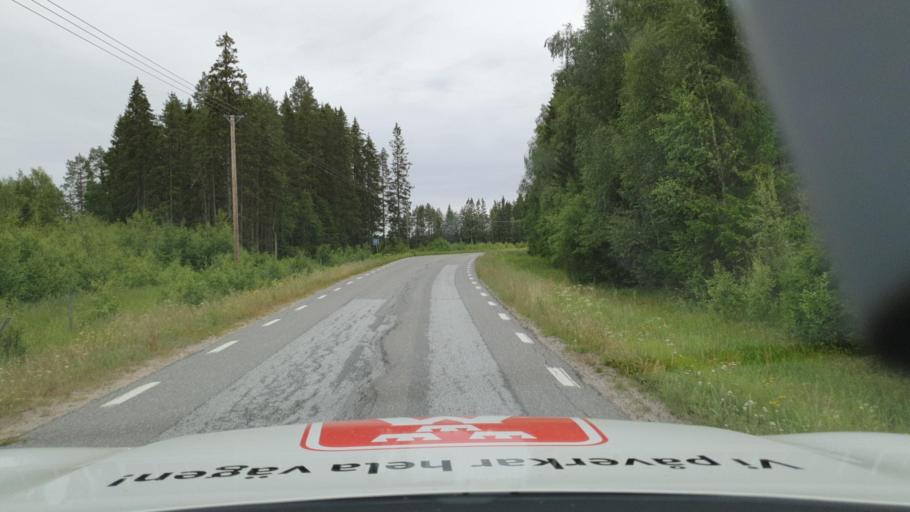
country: SE
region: Vaesterbotten
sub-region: Nordmalings Kommun
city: Nordmaling
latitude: 63.5103
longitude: 19.4211
